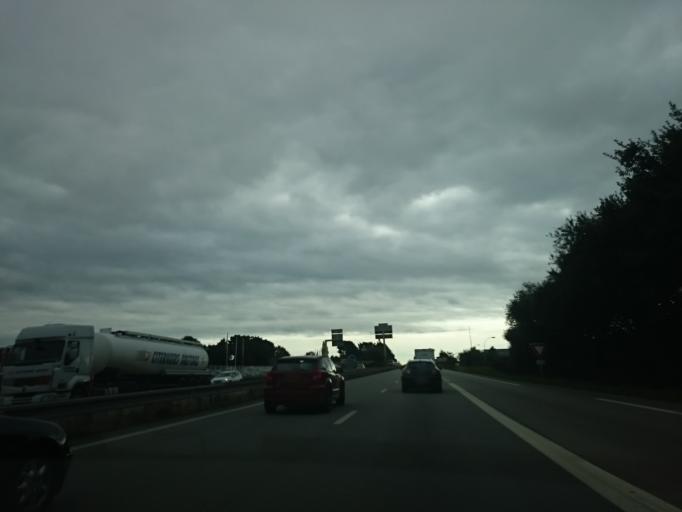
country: FR
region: Brittany
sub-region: Departement du Morbihan
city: Vannes
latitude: 47.6652
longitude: -2.7234
